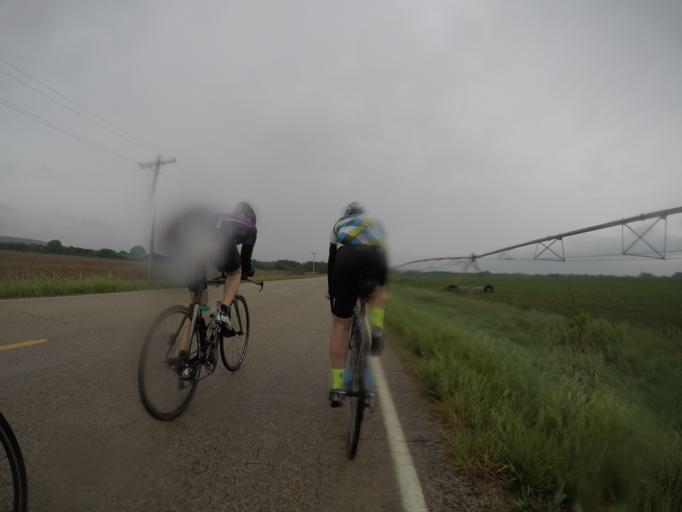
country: US
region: Kansas
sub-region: Pottawatomie County
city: Wamego
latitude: 39.3422
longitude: -96.2213
